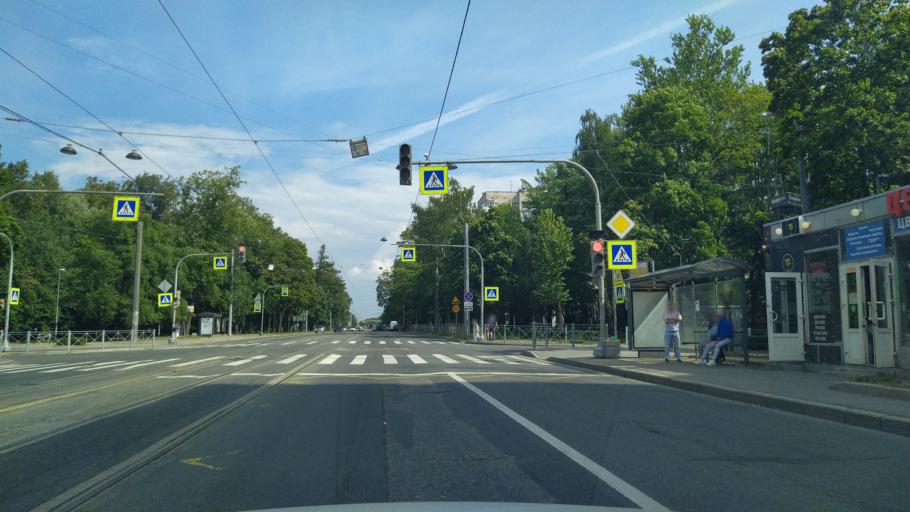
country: RU
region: St.-Petersburg
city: Kushelevka
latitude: 59.9998
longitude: 30.3525
